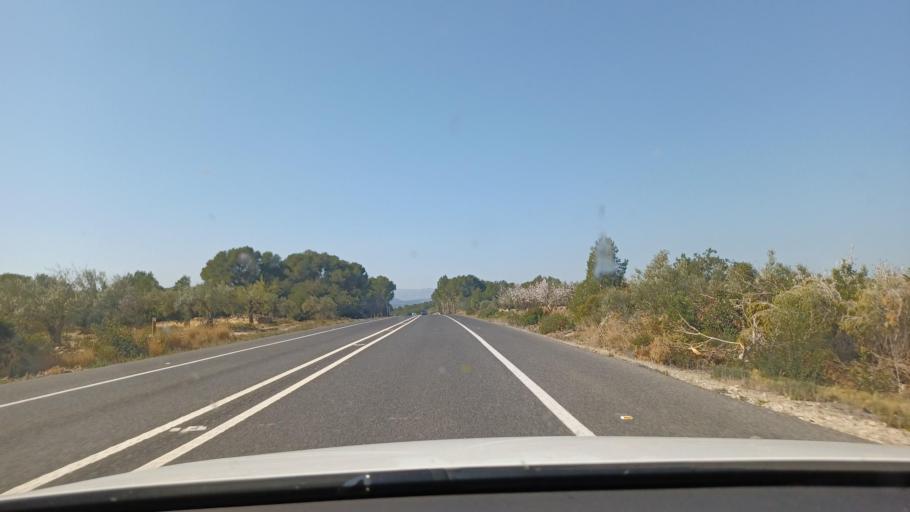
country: ES
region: Catalonia
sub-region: Provincia de Tarragona
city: l'Ametlla de Mar
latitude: 40.8943
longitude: 0.7736
